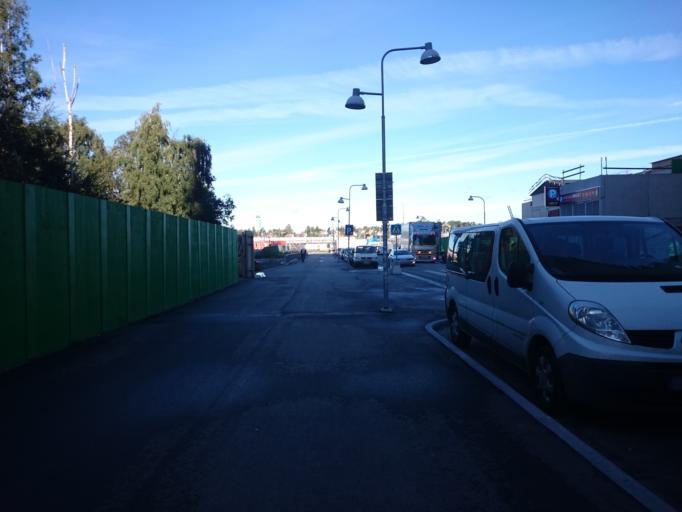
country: SE
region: Stockholm
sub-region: Solna Kommun
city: Solna
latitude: 59.3720
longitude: 17.9981
